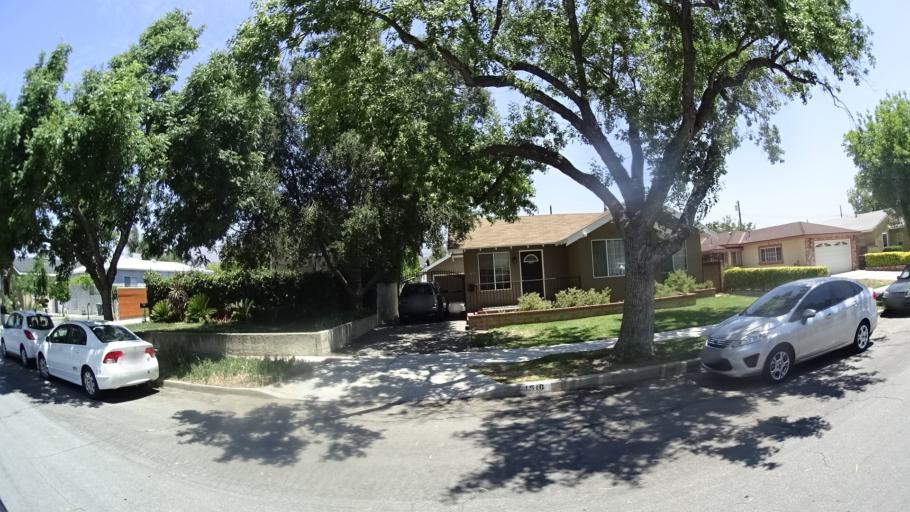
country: US
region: California
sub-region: Los Angeles County
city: Burbank
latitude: 34.1778
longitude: -118.3364
